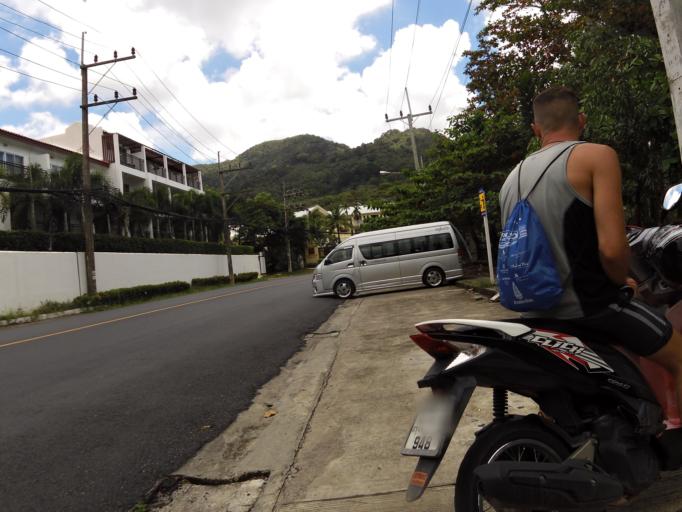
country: TH
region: Phuket
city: Ban Karon
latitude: 7.8535
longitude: 98.2932
